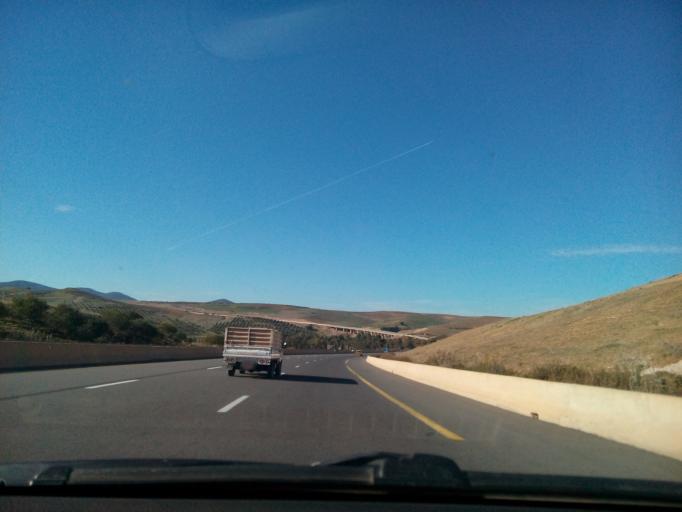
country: DZ
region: Tlemcen
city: Sidi Abdelli
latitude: 35.0379
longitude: -1.0525
